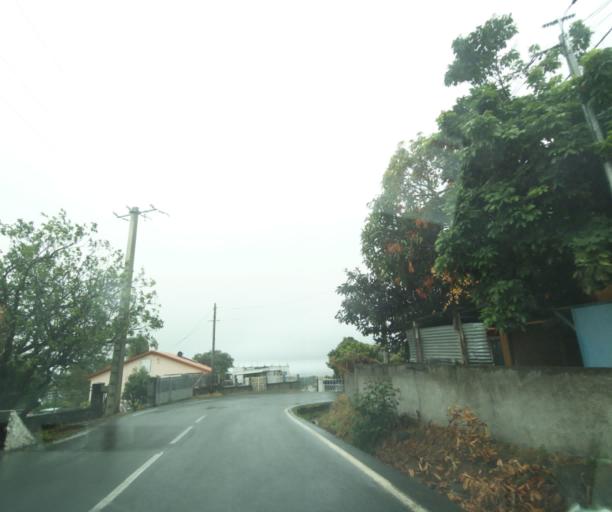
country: RE
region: Reunion
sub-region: Reunion
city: Saint-Paul
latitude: -21.0258
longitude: 55.2866
